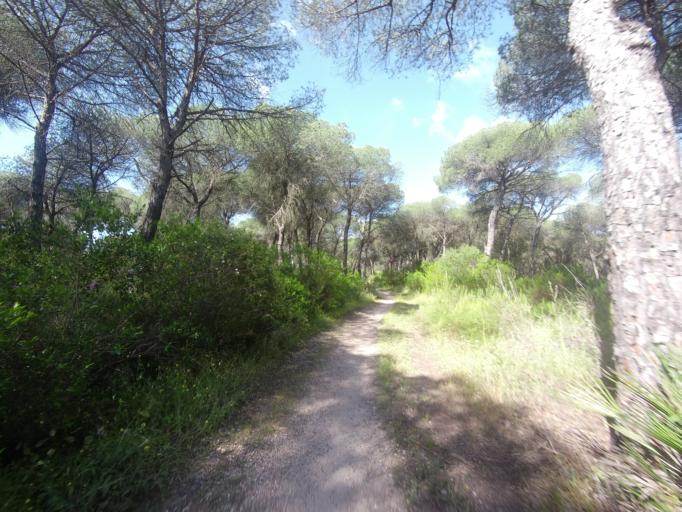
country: ES
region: Andalusia
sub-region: Provincia de Huelva
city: Aljaraque
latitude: 37.2339
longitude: -7.0468
